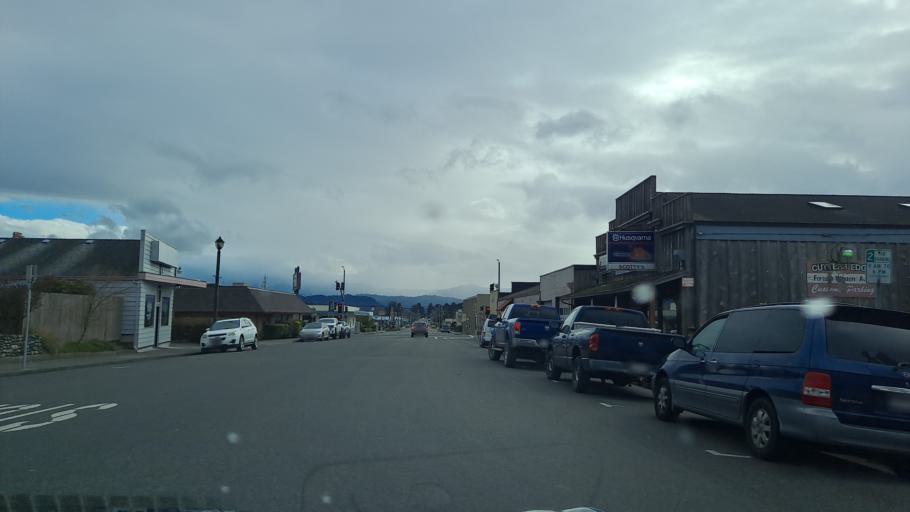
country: US
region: California
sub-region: Humboldt County
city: Fortuna
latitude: 40.5988
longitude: -124.1545
